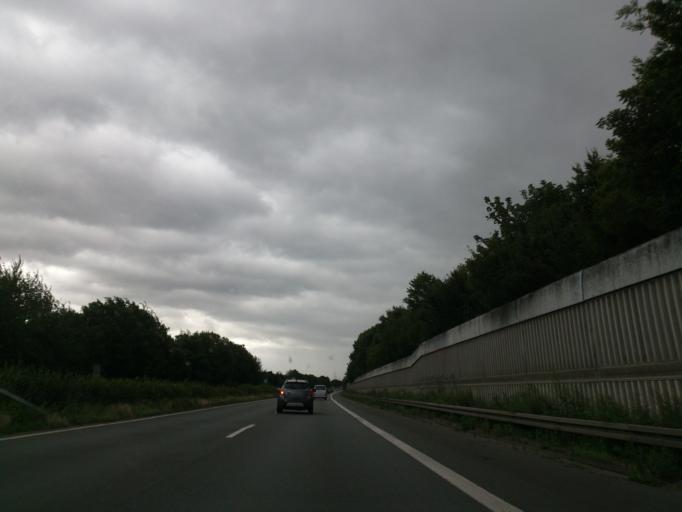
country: DE
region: North Rhine-Westphalia
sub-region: Regierungsbezirk Detmold
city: Paderborn
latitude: 51.7265
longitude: 8.7059
